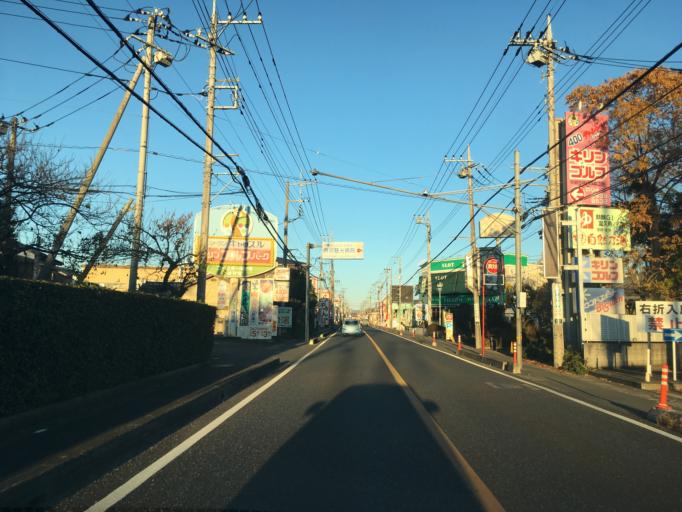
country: JP
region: Saitama
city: Tokorozawa
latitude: 35.8108
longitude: 139.4307
